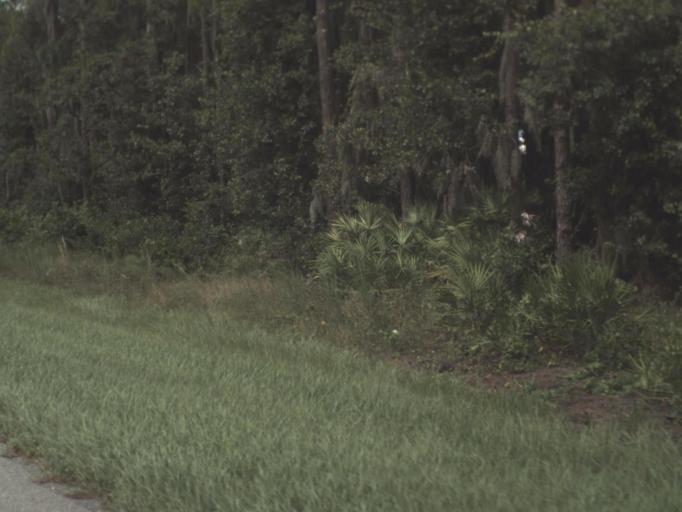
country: US
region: Florida
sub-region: Hillsborough County
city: Balm
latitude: 27.6069
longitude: -82.0999
